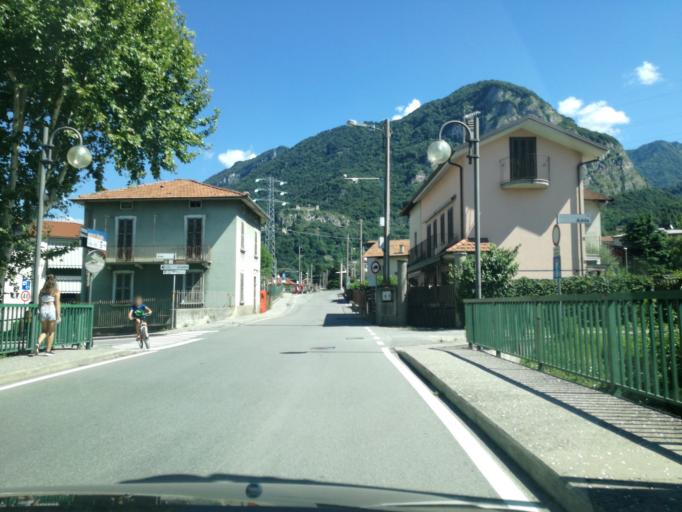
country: IT
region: Lombardy
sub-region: Provincia di Lecco
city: Vercurago
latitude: 45.8065
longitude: 9.4199
